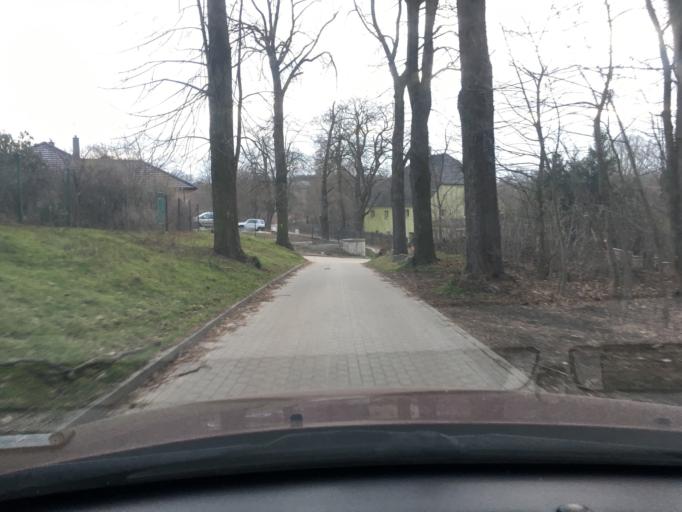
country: PL
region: Lower Silesian Voivodeship
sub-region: Powiat zgorzelecki
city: Zgorzelec
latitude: 51.1425
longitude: 14.9976
